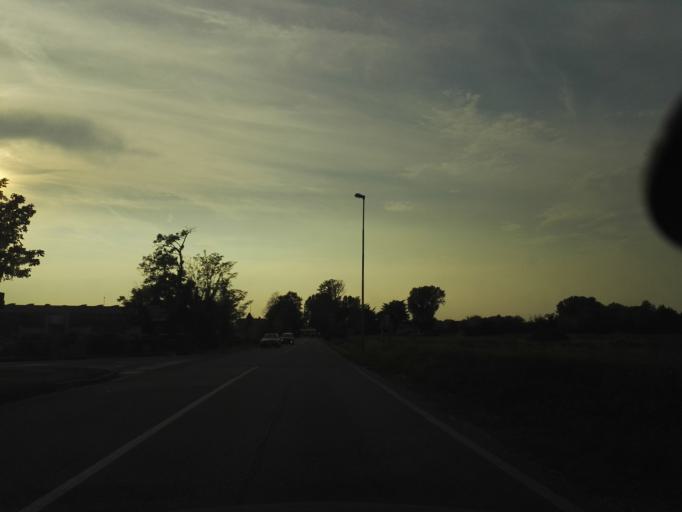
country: IT
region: Lombardy
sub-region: Citta metropolitana di Milano
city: Mezzate
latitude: 45.4369
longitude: 9.2939
